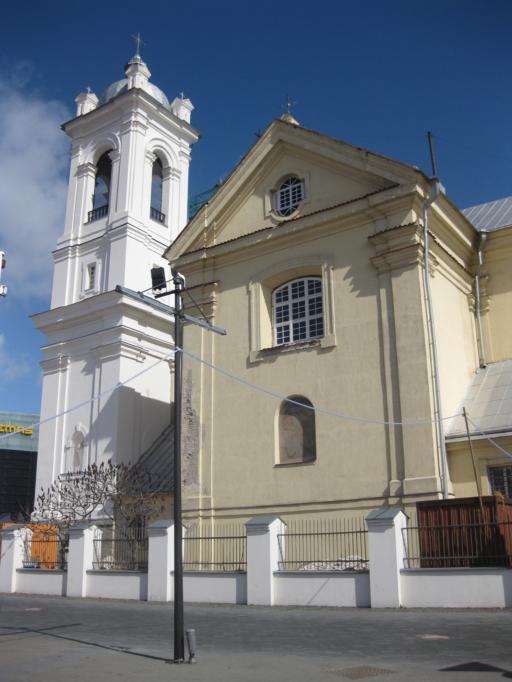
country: LT
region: Kauno apskritis
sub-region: Kaunas
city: Aleksotas
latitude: 54.8900
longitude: 23.9196
